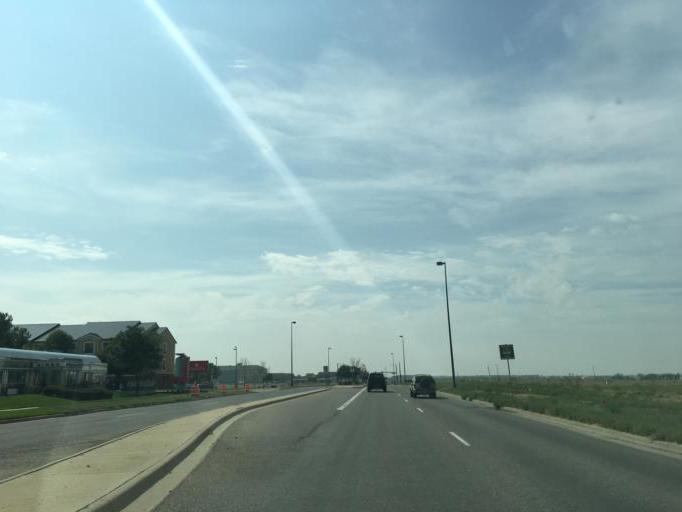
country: US
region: Colorado
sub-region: Adams County
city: Aurora
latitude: 39.8107
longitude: -104.7722
